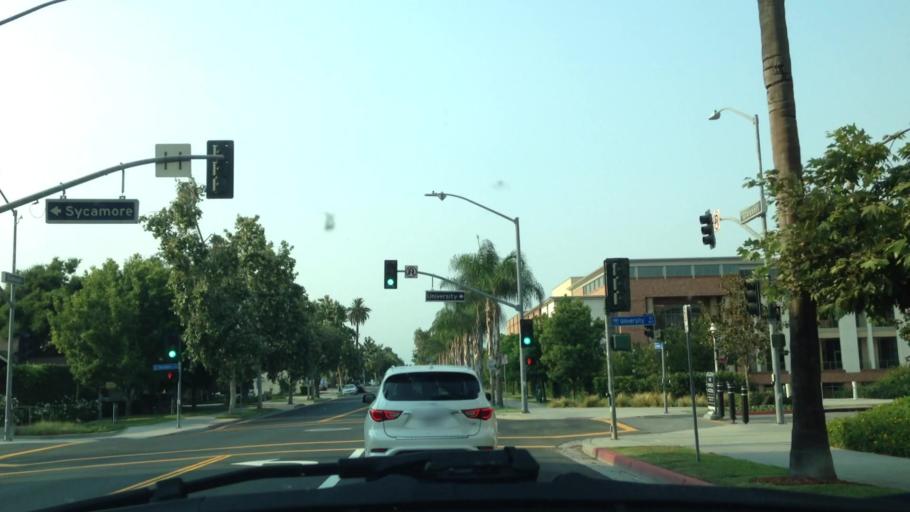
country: US
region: California
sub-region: Orange County
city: Orange
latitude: 33.7930
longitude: -117.8531
